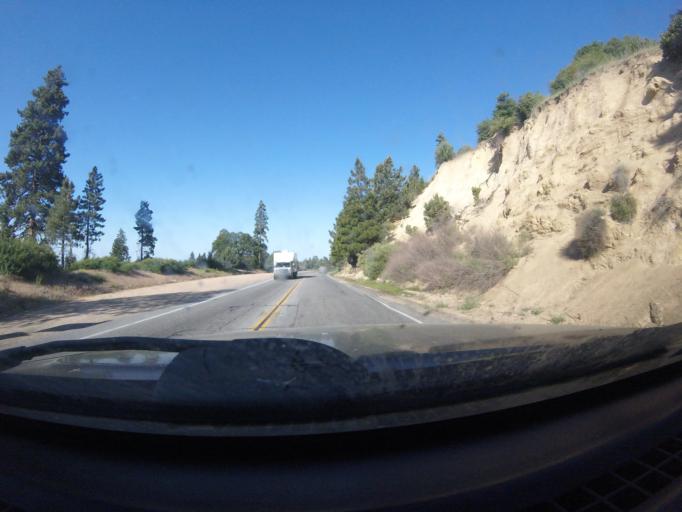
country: US
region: California
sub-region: San Bernardino County
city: Running Springs
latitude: 34.2056
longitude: -117.1282
